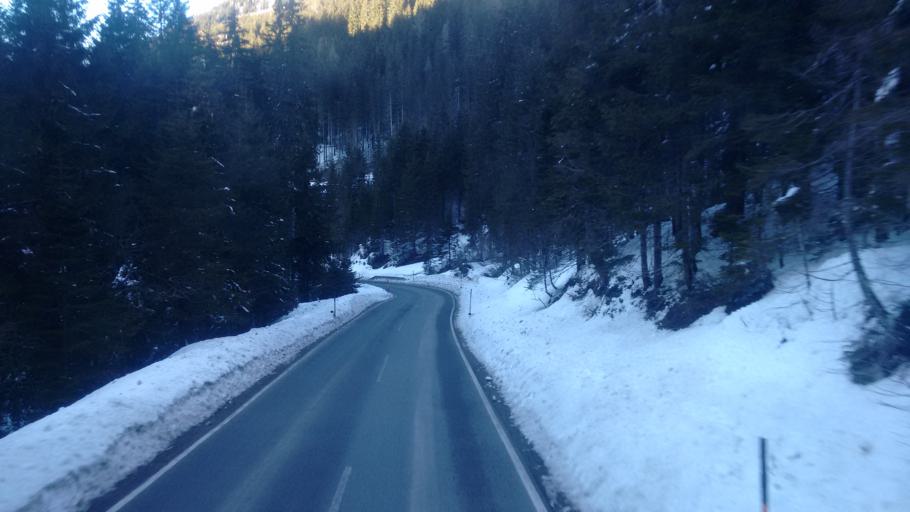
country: AT
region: Salzburg
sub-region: Politischer Bezirk Sankt Johann im Pongau
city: Untertauern
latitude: 47.3017
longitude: 13.4566
